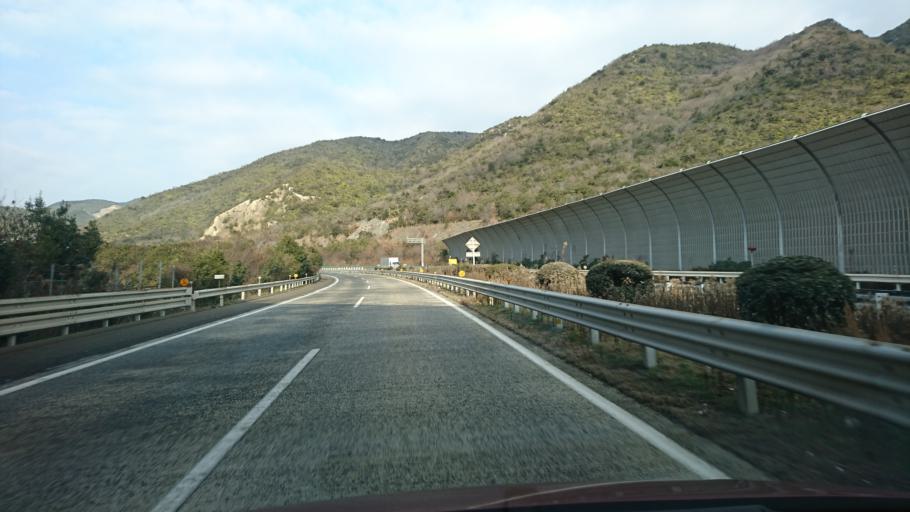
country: JP
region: Hyogo
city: Kariya
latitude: 34.7791
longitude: 134.3452
